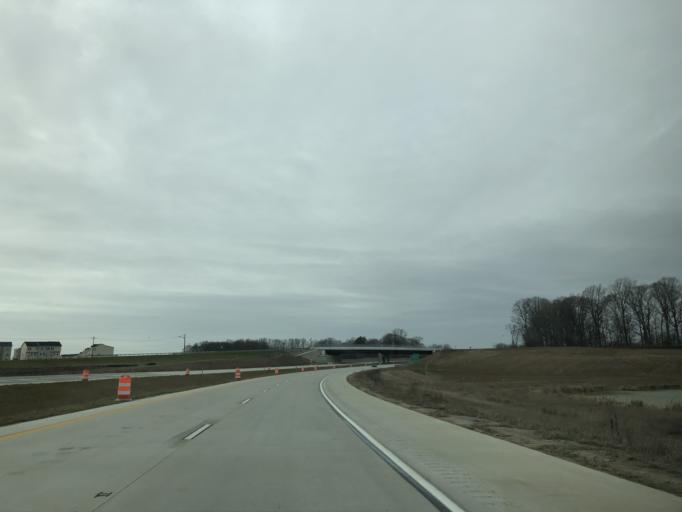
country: US
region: Delaware
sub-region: New Castle County
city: Delaware City
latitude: 39.5256
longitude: -75.6596
